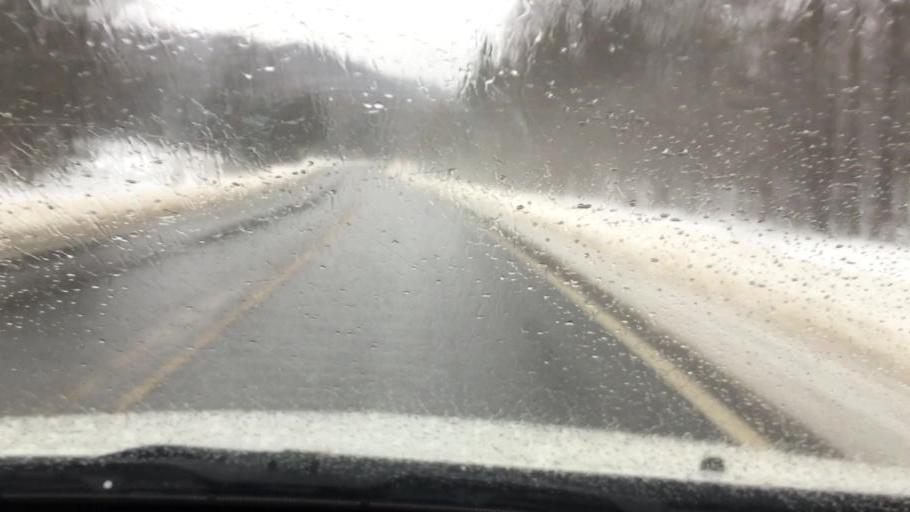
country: US
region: Michigan
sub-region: Antrim County
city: Mancelona
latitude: 45.0072
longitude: -85.0641
